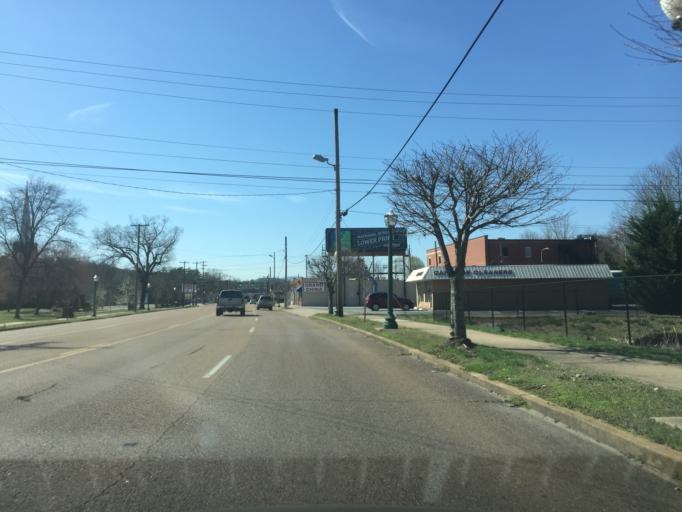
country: US
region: Tennessee
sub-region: Hamilton County
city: Red Bank
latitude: 35.1185
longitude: -85.2905
